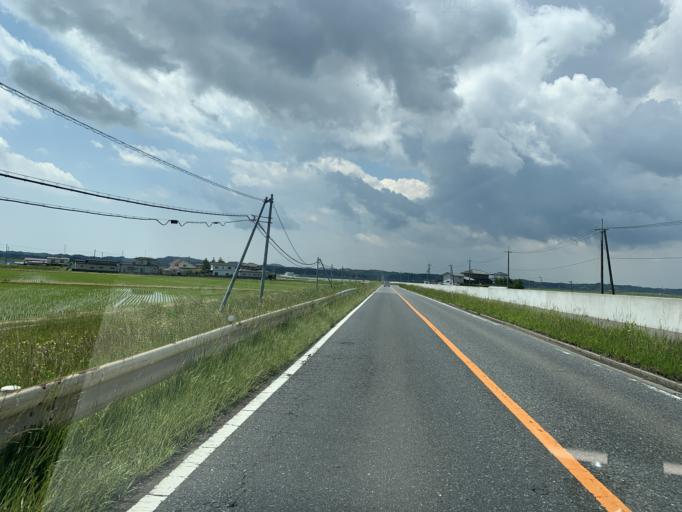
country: JP
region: Miyagi
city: Matsushima
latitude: 38.4516
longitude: 141.0828
